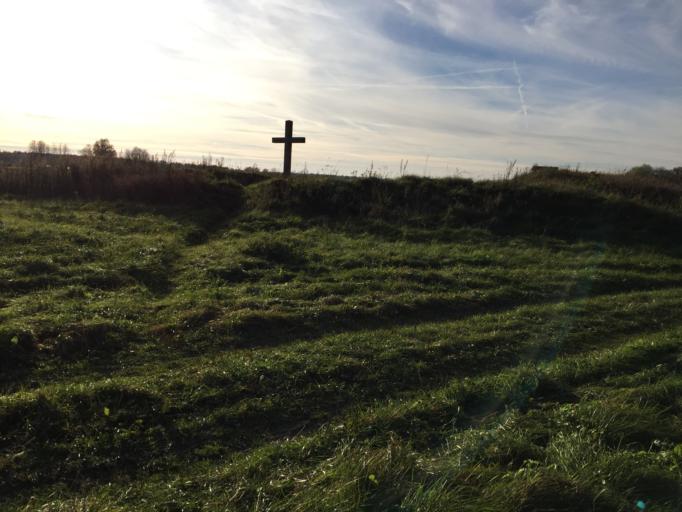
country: LV
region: Skriveri
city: Skriveri
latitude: 56.6211
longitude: 25.1292
